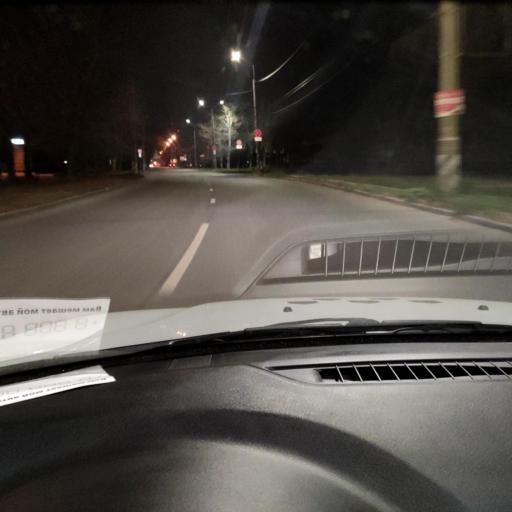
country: RU
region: Samara
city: Tol'yatti
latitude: 53.5140
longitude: 49.4549
